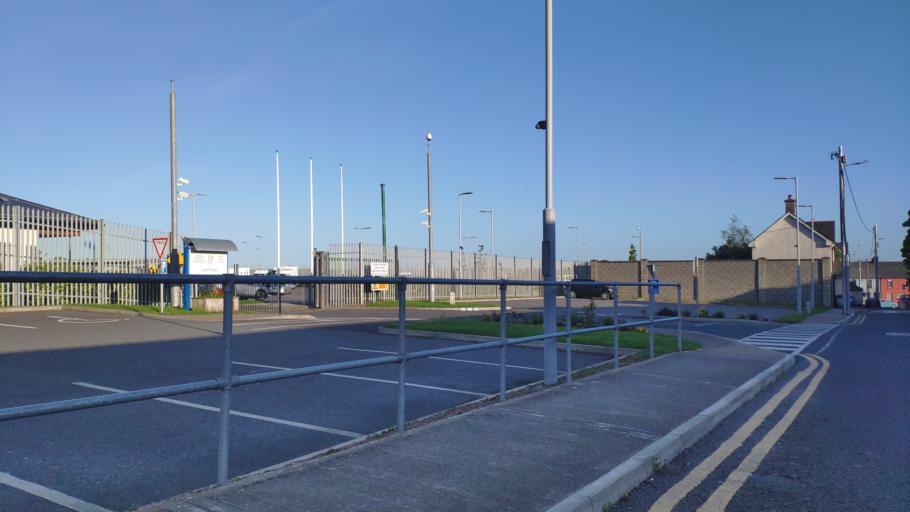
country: IE
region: Munster
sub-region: County Cork
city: Cork
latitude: 51.9084
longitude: -8.4606
